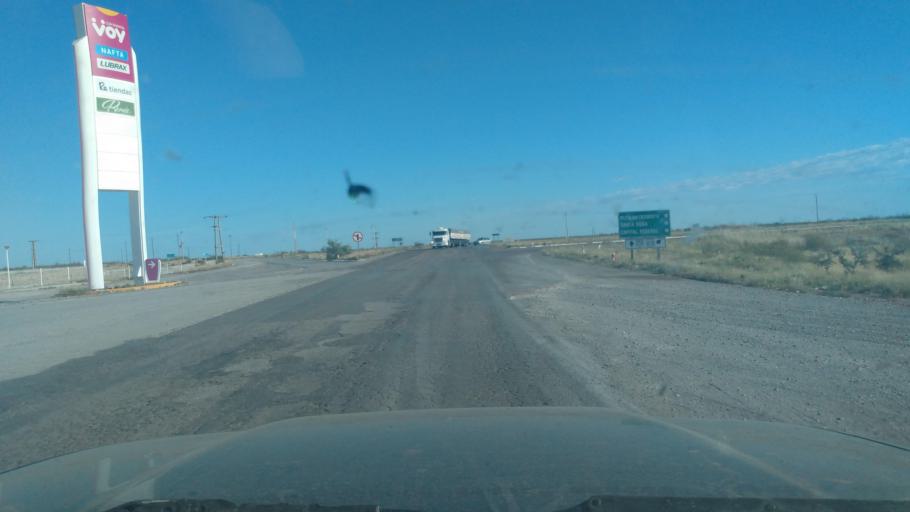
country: AR
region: La Pampa
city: Veinticinco de Mayo
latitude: -37.6612
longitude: -67.7492
